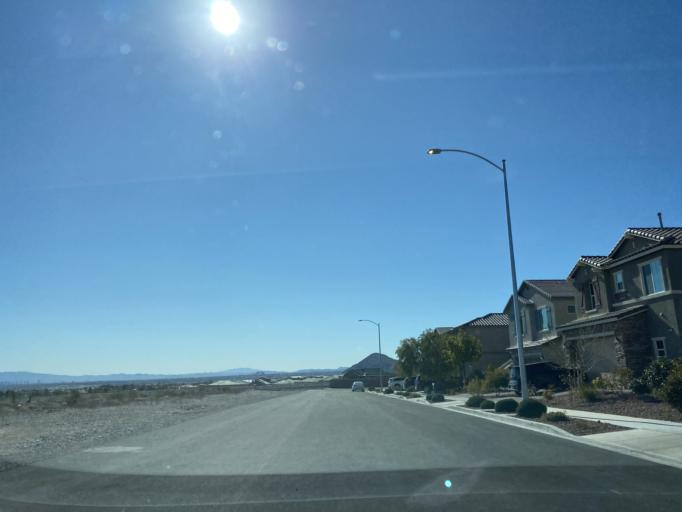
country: US
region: Nevada
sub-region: Clark County
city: Summerlin South
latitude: 36.2827
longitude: -115.3104
